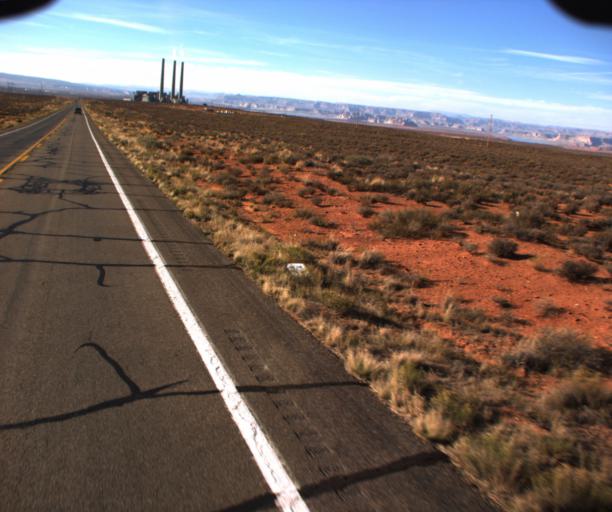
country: US
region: Arizona
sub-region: Coconino County
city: LeChee
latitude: 36.8864
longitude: -111.3608
